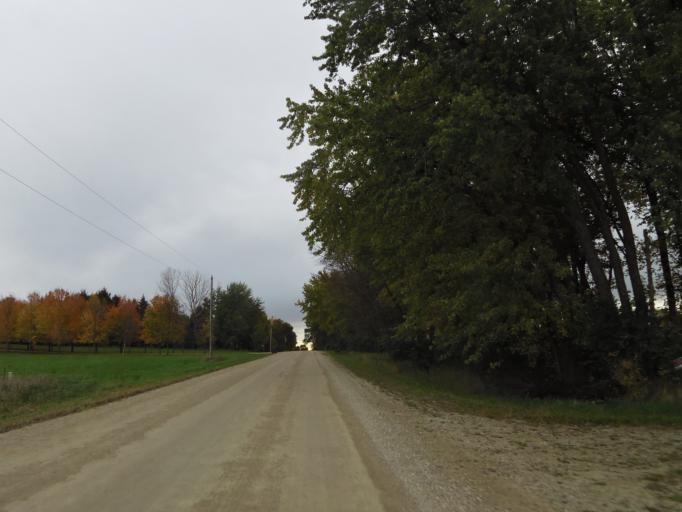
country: US
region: Minnesota
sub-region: Scott County
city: Prior Lake
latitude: 44.7035
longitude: -93.5097
